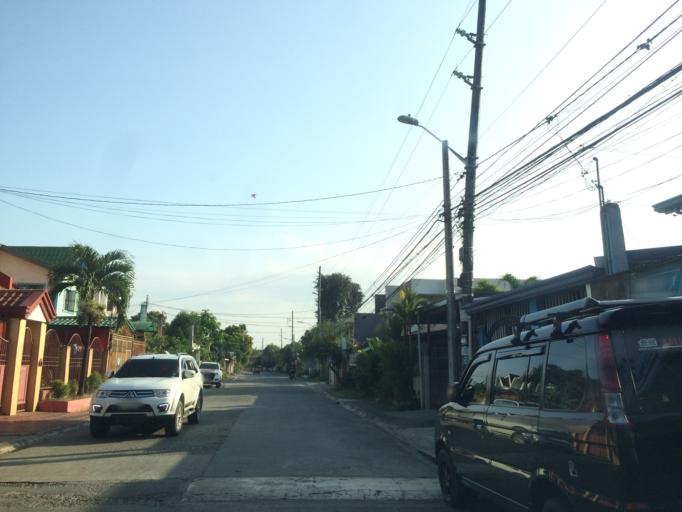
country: PH
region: Calabarzon
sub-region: Province of Rizal
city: San Mateo
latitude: 14.6788
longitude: 121.1220
